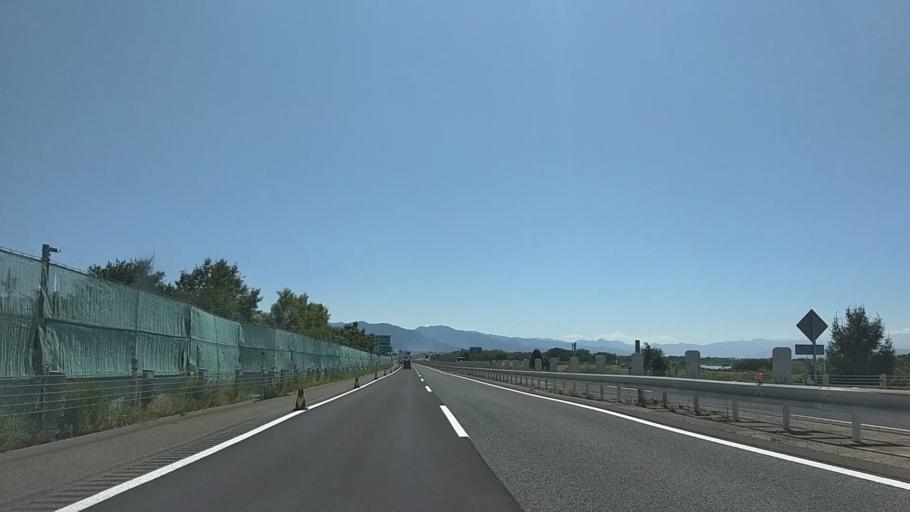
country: JP
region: Nagano
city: Nakano
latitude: 36.7218
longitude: 138.3145
